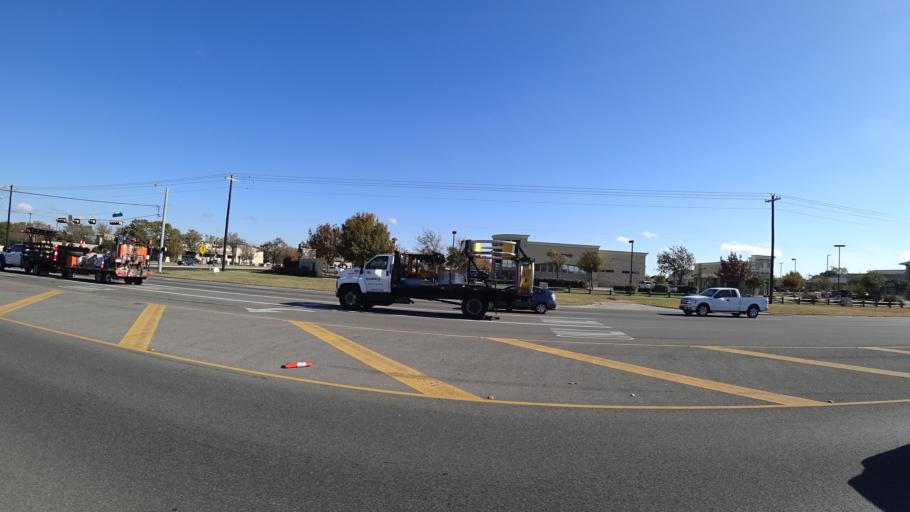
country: US
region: Texas
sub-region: Williamson County
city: Brushy Creek
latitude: 30.4977
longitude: -97.7756
